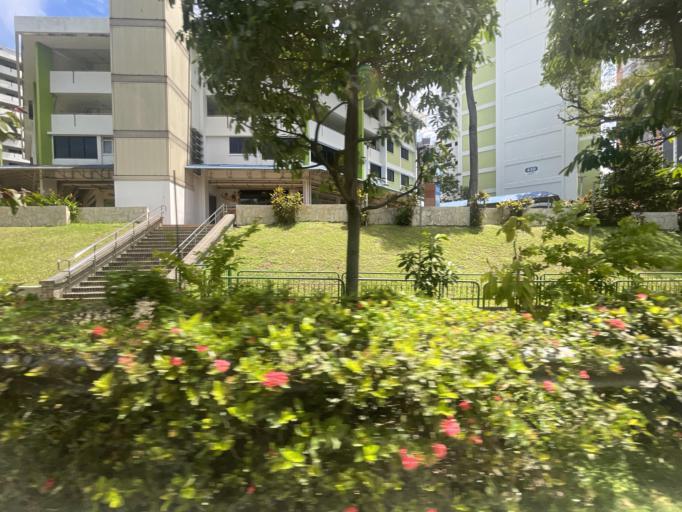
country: SG
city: Singapore
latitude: 1.3132
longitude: 103.7619
